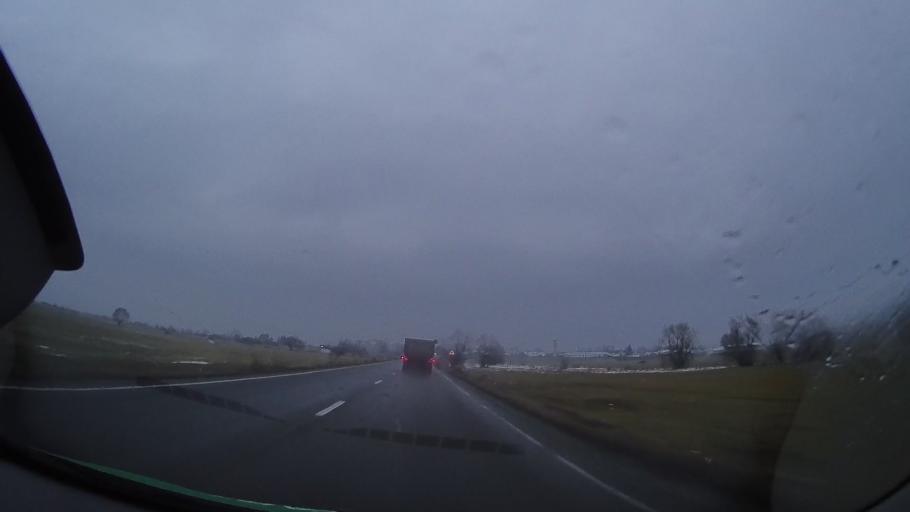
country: RO
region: Harghita
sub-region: Comuna Lazarea
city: Lazarea
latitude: 46.7611
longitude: 25.5156
